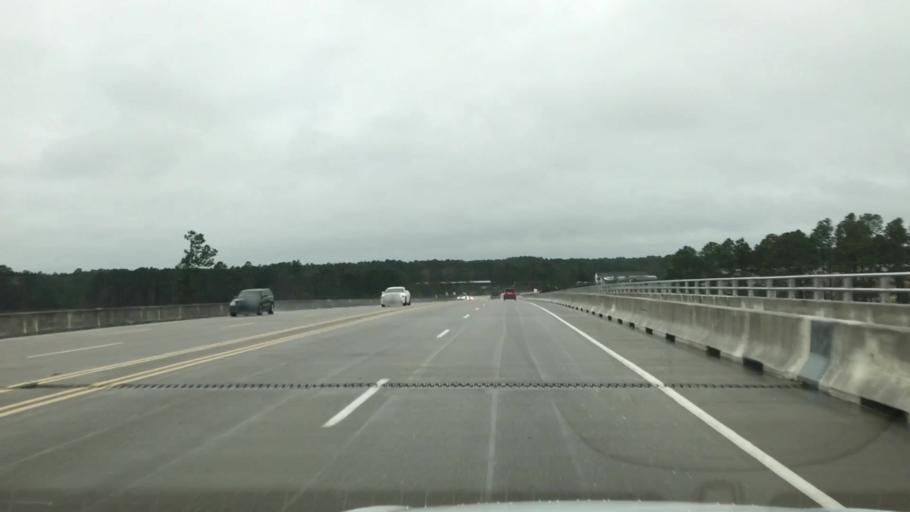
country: US
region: South Carolina
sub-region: Horry County
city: Forestbrook
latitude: 33.7060
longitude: -78.9353
